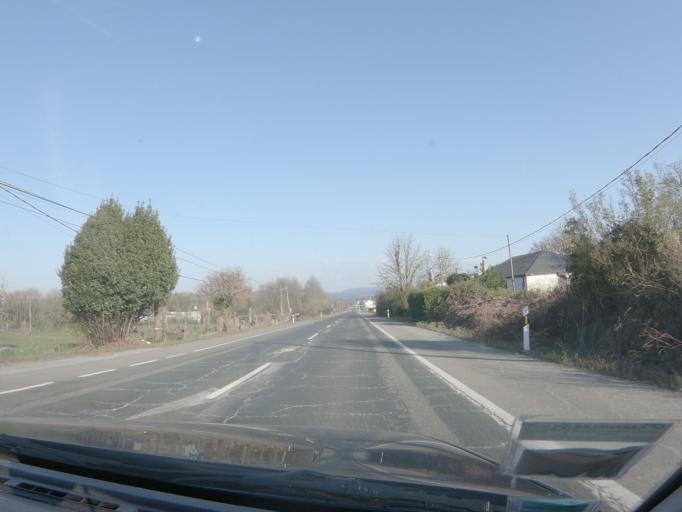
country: ES
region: Galicia
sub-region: Provincia de Lugo
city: Corgo
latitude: 42.9503
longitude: -7.4539
